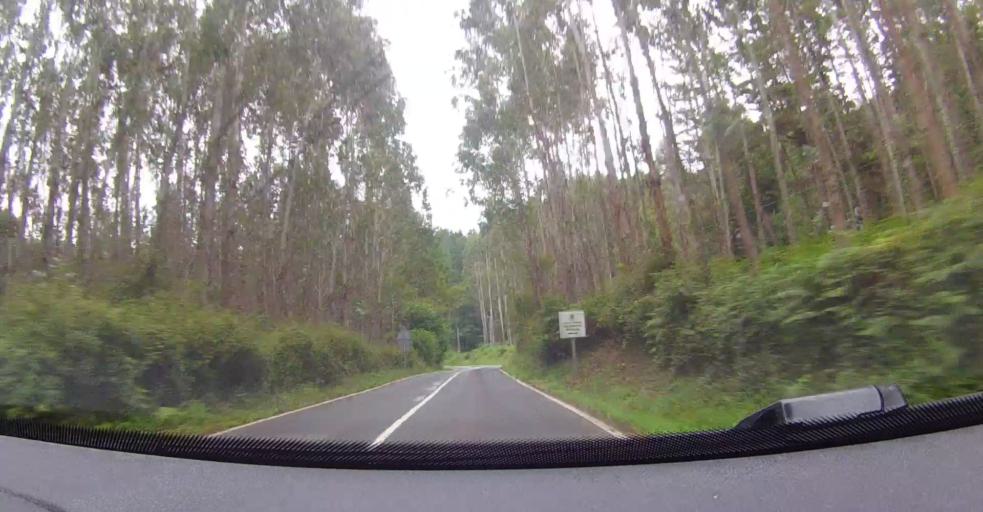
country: ES
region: Basque Country
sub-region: Bizkaia
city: Balmaseda
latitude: 43.2404
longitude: -3.2424
